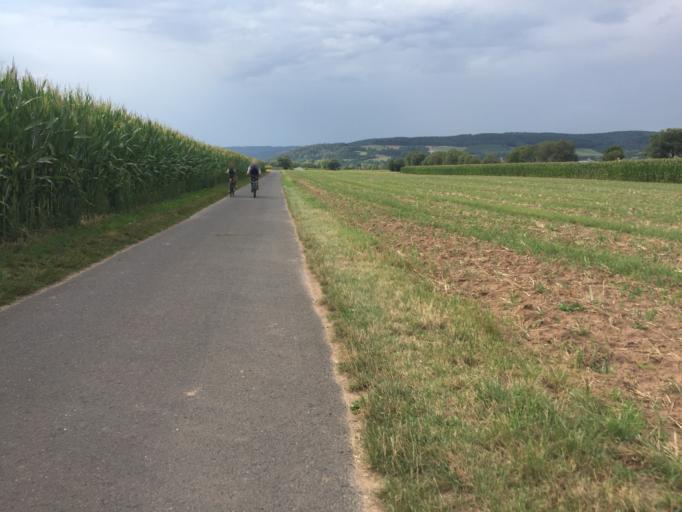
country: DE
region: Hesse
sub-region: Regierungsbezirk Kassel
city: Alheim
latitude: 51.0369
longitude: 9.6691
